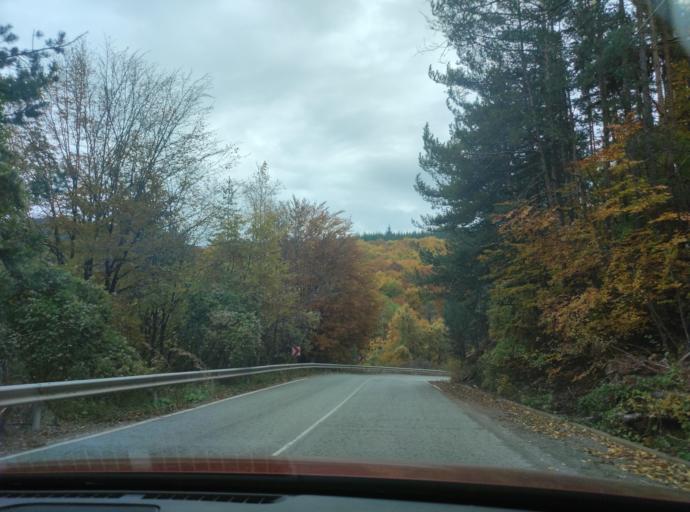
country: BG
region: Sofiya
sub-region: Obshtina Godech
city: Godech
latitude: 43.0213
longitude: 23.1338
